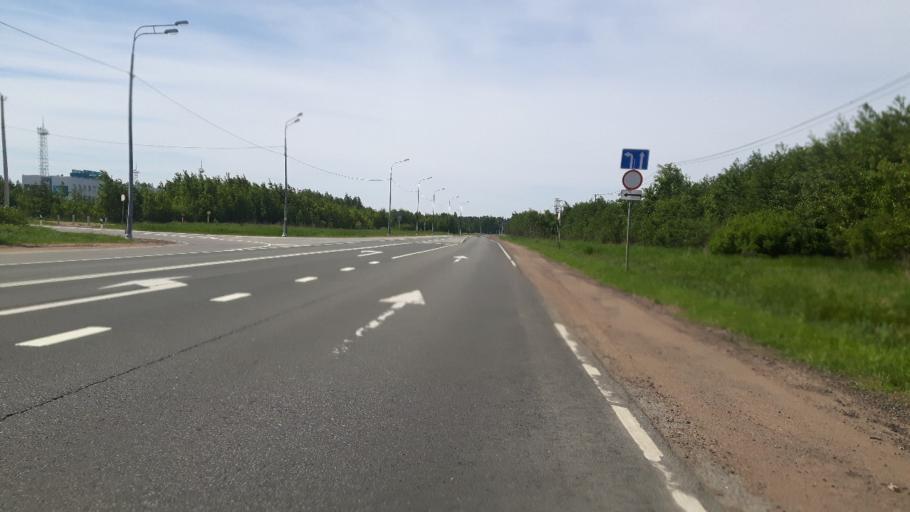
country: RU
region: Leningrad
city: Ust'-Luga
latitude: 59.6546
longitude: 28.3807
